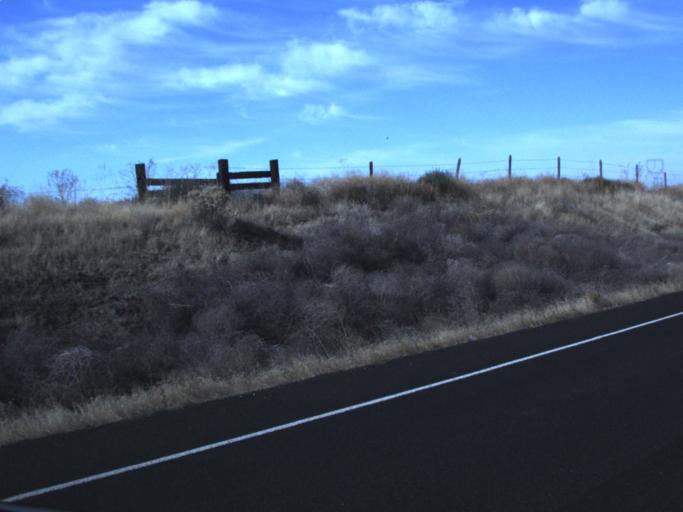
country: US
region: Washington
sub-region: Franklin County
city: Connell
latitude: 46.6382
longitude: -118.8161
